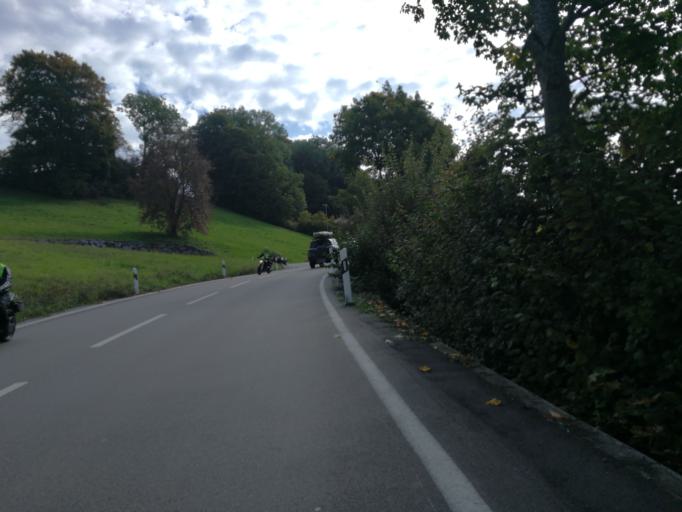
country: CH
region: Zurich
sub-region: Bezirk Meilen
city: Mannedorf
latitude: 47.2590
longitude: 8.7053
